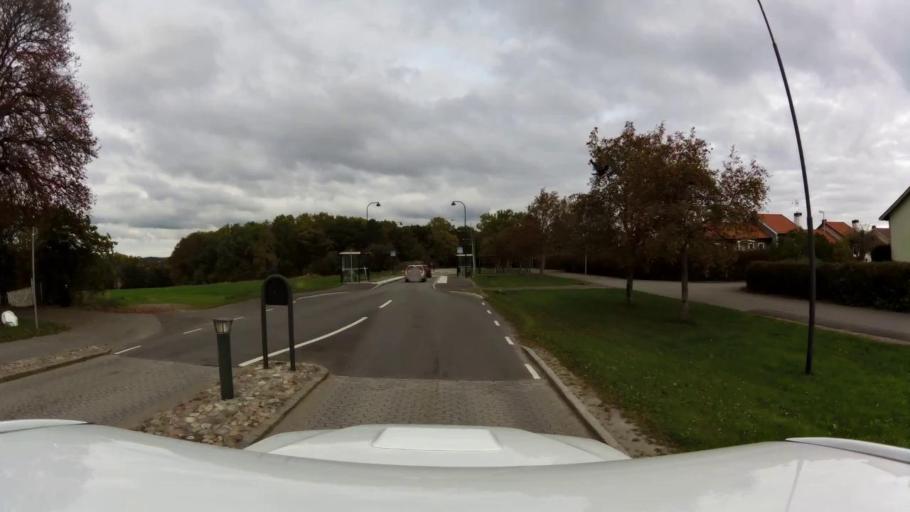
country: SE
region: OEstergoetland
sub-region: Linkopings Kommun
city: Berg
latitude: 58.4906
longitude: 15.5270
